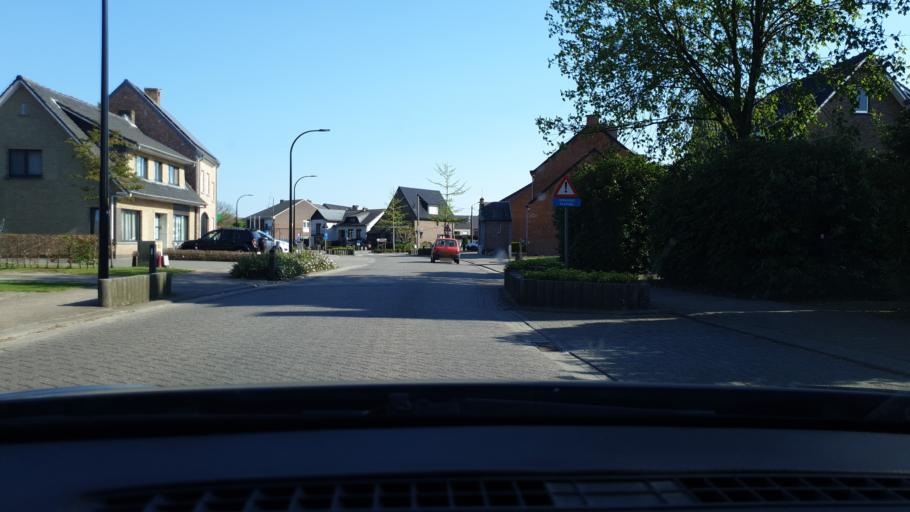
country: BE
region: Flanders
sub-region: Provincie Antwerpen
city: Geel
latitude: 51.1658
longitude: 4.9469
